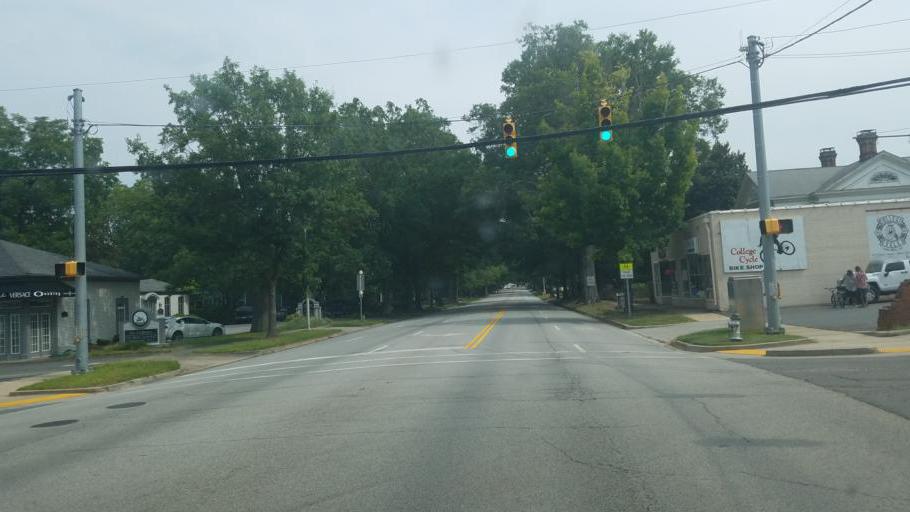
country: US
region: South Carolina
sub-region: York County
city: Rock Hill
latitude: 34.9354
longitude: -81.0270
